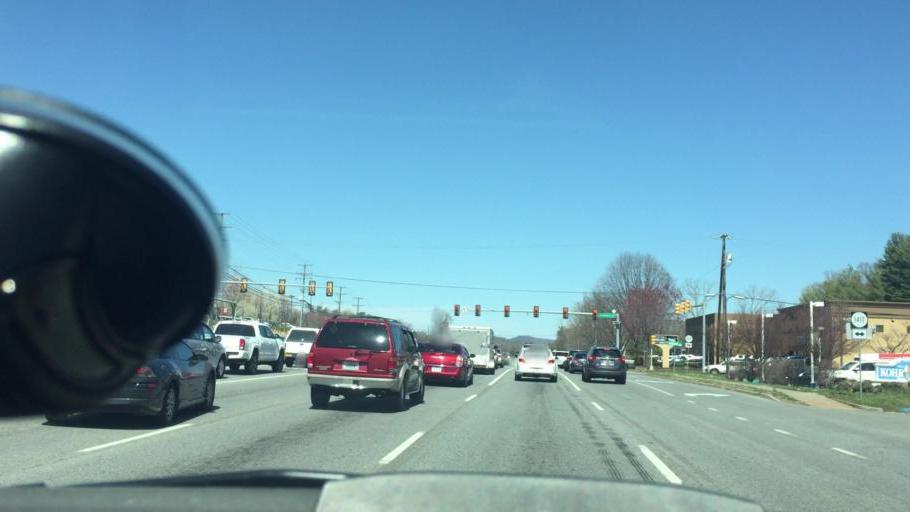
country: US
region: Virginia
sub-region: Albemarle County
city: Hollymead
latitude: 38.0871
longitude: -78.4707
